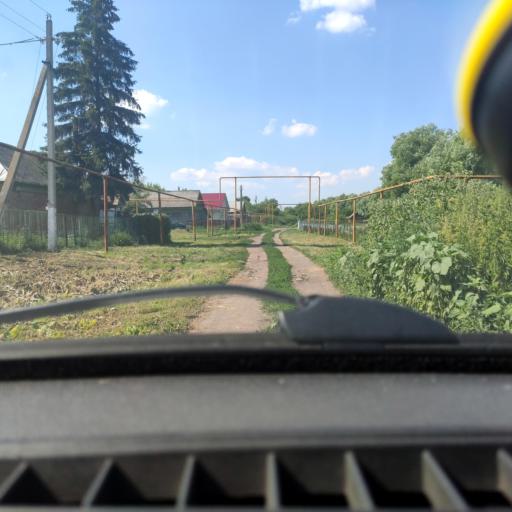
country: RU
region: Samara
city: Povolzhskiy
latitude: 53.7586
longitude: 49.7322
